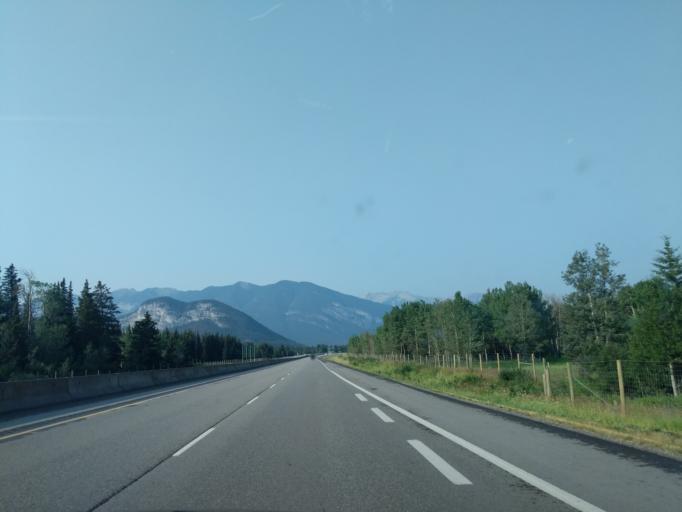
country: CA
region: Alberta
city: Banff
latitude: 51.2023
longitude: -115.5436
